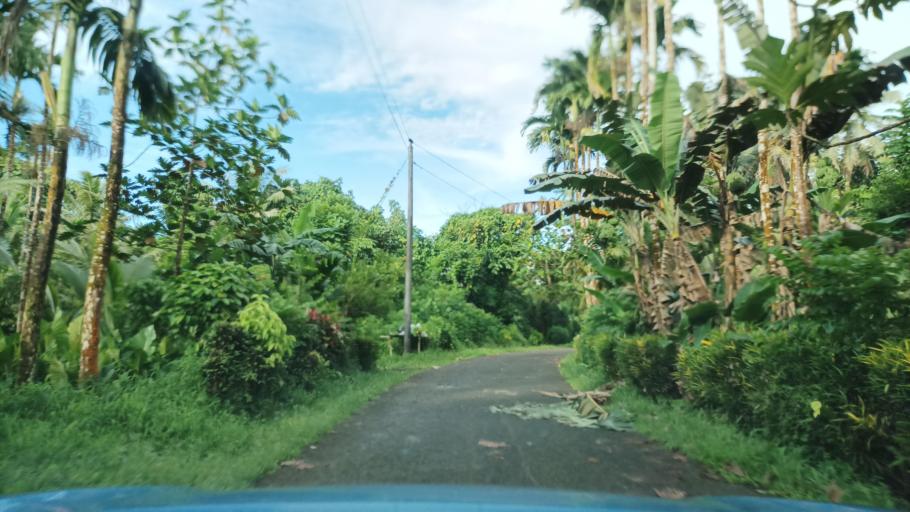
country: FM
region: Pohnpei
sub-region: Sokehs Municipality
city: Palikir - National Government Center
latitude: 6.9160
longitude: 158.1429
